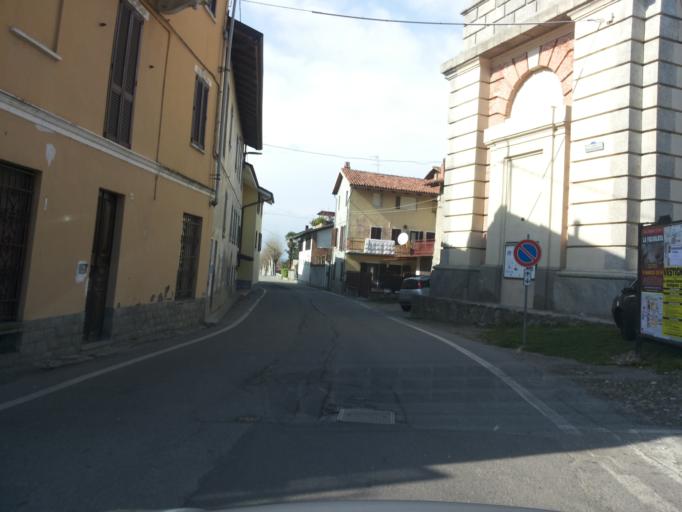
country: IT
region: Piedmont
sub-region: Provincia di Torino
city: Vestigne
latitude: 45.3874
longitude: 7.9530
